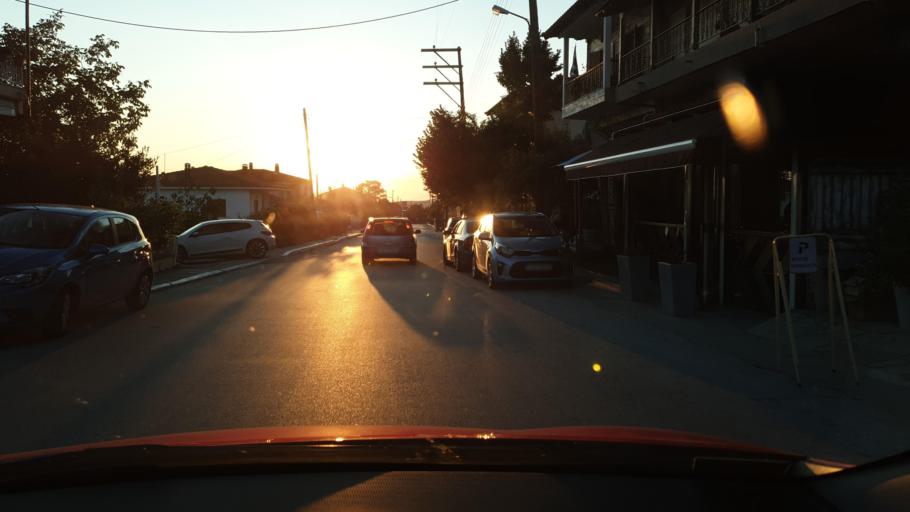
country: GR
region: Central Macedonia
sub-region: Nomos Chalkidikis
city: Galatista
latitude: 40.4675
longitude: 23.2759
